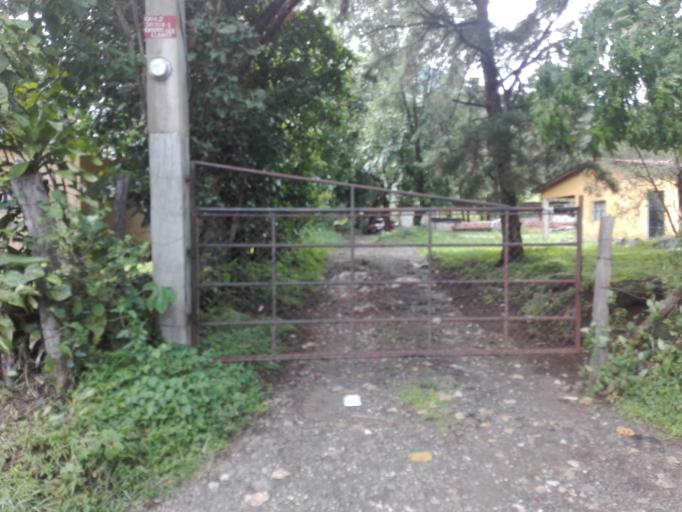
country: GT
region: Escuintla
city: San Vicente Pacaya
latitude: 14.3719
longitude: -90.5594
